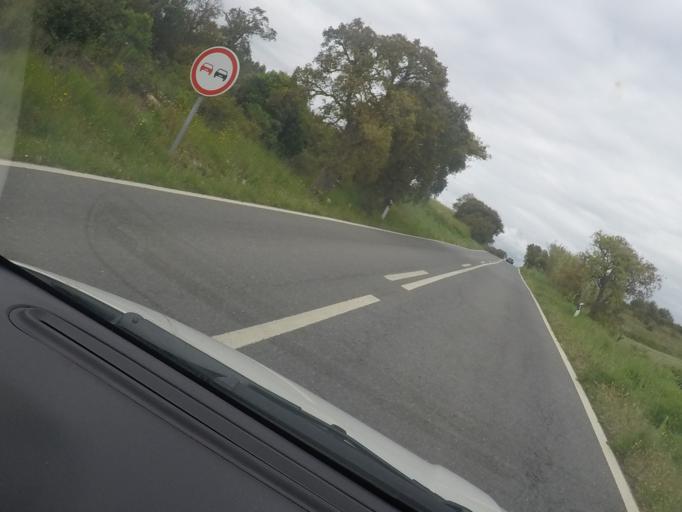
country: PT
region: Setubal
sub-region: Santiago do Cacem
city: Cercal
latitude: 37.7926
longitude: -8.6943
